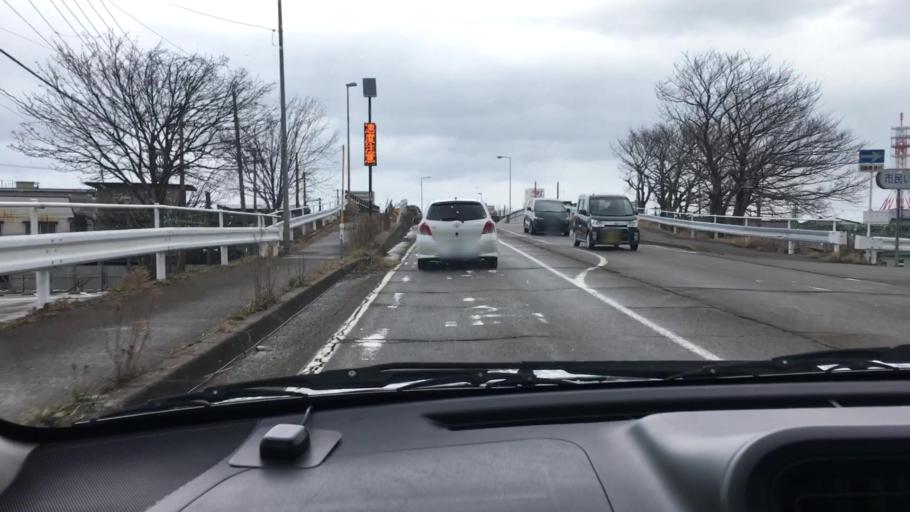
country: JP
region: Niigata
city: Joetsu
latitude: 37.1665
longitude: 138.2371
